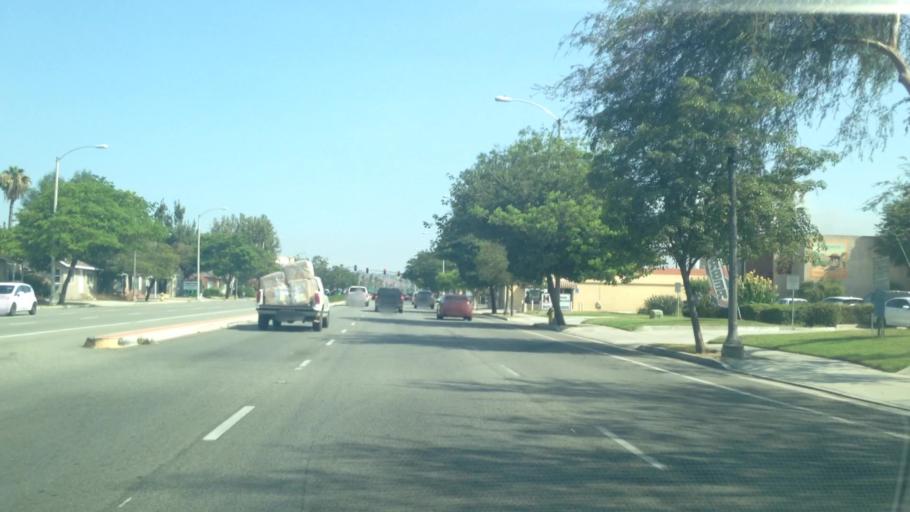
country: US
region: California
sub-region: Riverside County
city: Riverside
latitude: 33.9189
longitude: -117.4454
